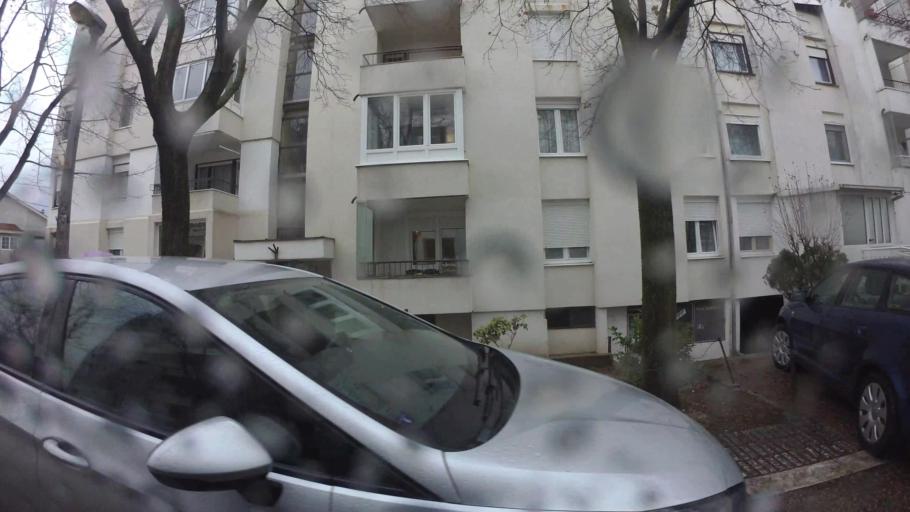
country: BA
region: Federation of Bosnia and Herzegovina
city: Cim
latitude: 43.3466
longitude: 17.7919
